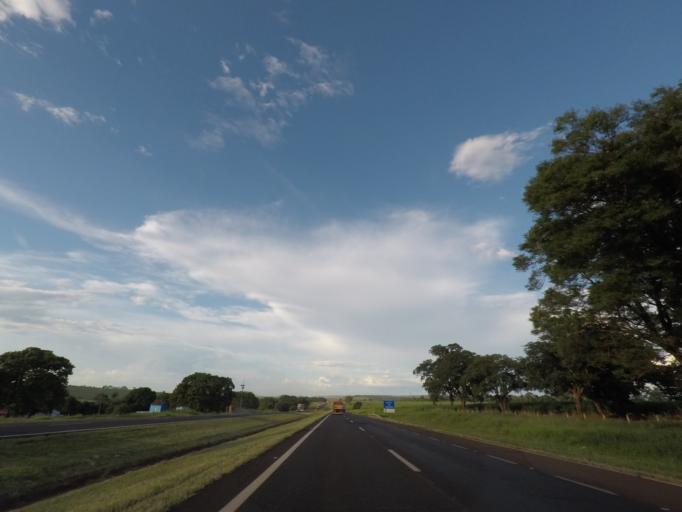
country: BR
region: Sao Paulo
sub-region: Ituverava
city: Ituverava
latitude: -20.3171
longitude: -47.8023
